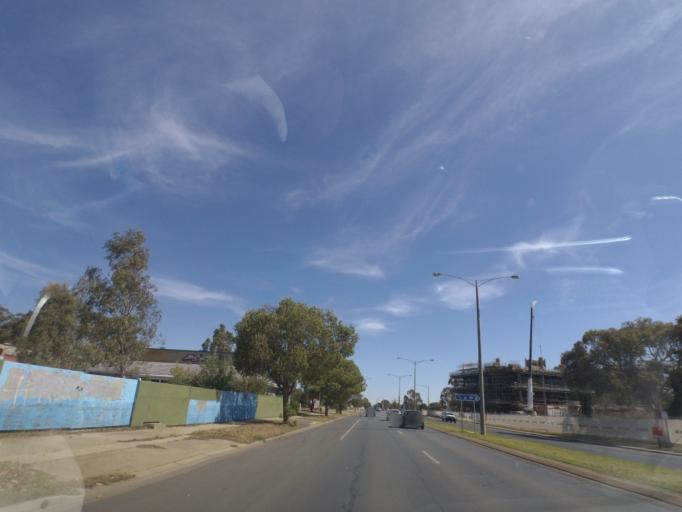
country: AU
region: Victoria
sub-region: Greater Shepparton
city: Shepparton
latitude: -36.3899
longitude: 145.3976
